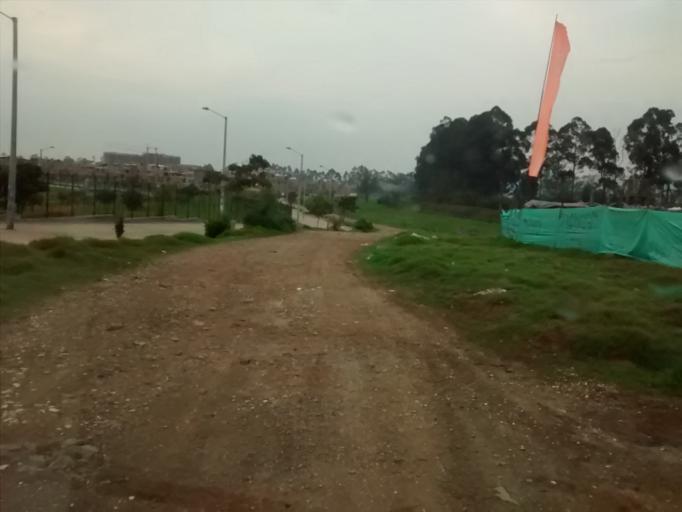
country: CO
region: Cundinamarca
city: Cota
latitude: 4.7573
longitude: -74.1095
